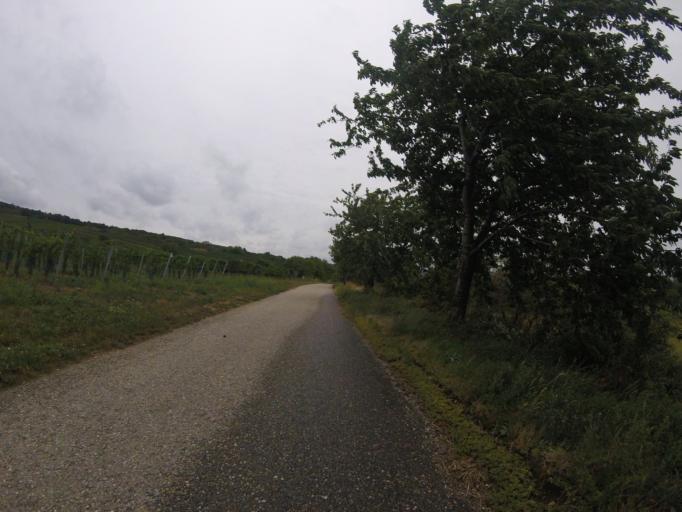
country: AT
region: Burgenland
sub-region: Eisenstadt-Umgebung
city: Breitenbrunn
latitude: 47.9414
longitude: 16.7074
